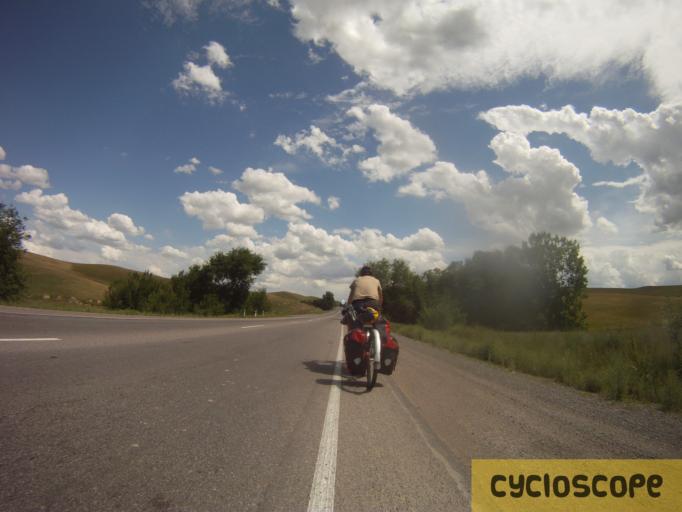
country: KZ
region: Almaty Oblysy
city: Burunday
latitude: 43.2979
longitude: 76.2288
